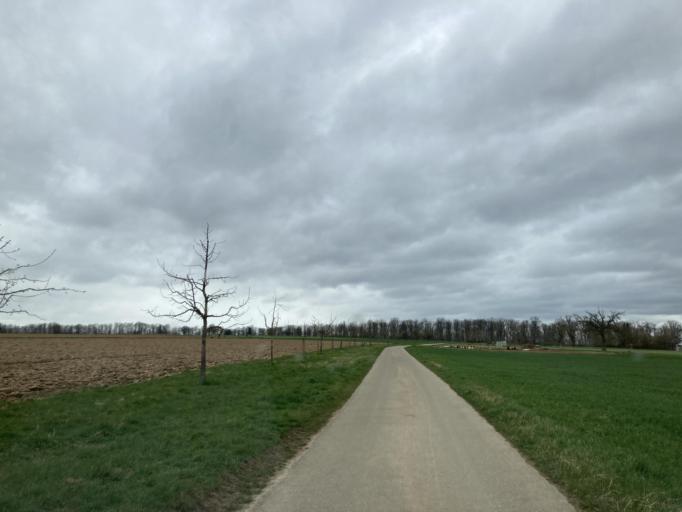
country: DE
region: Baden-Wuerttemberg
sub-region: Tuebingen Region
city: Gomaringen
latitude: 48.4944
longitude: 9.0877
